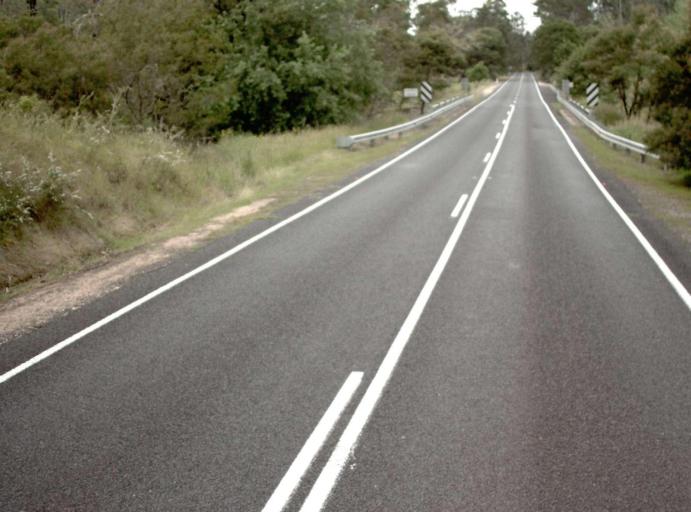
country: AU
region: New South Wales
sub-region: Bombala
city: Bombala
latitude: -37.4125
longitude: 149.1977
